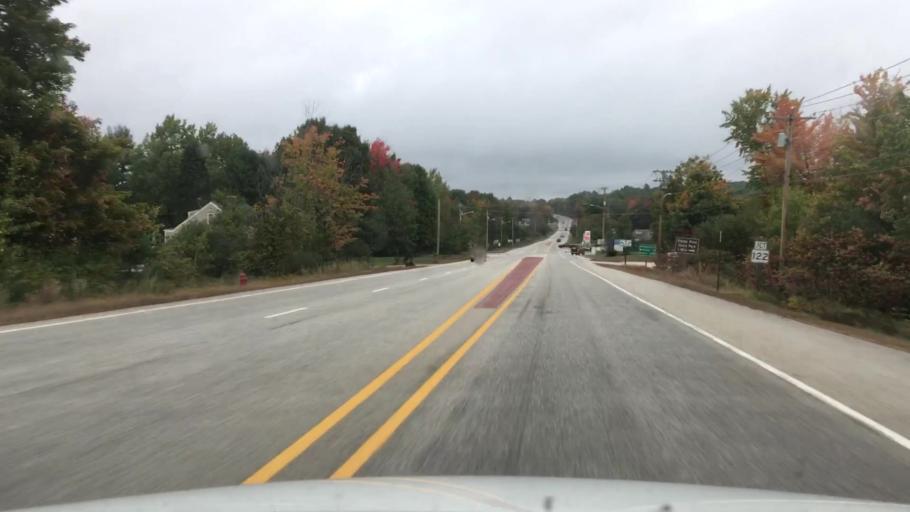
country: US
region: Maine
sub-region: Androscoggin County
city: Poland
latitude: 44.0115
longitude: -70.3624
